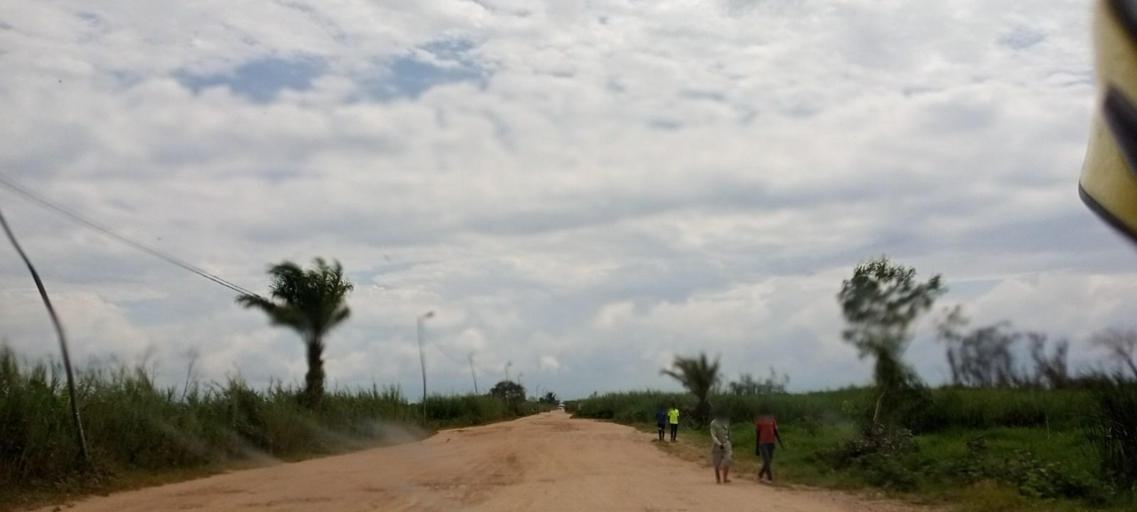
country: CD
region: South Kivu
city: Uvira
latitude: -3.3392
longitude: 29.2050
